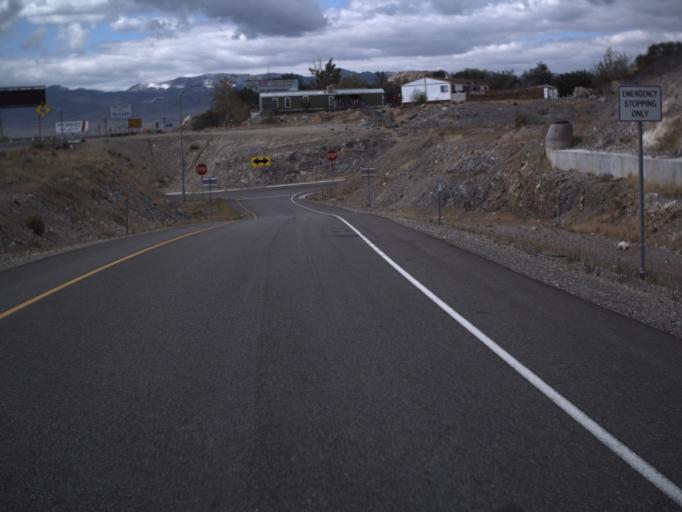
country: US
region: Utah
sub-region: Tooele County
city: Wendover
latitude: 40.7386
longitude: -114.0412
